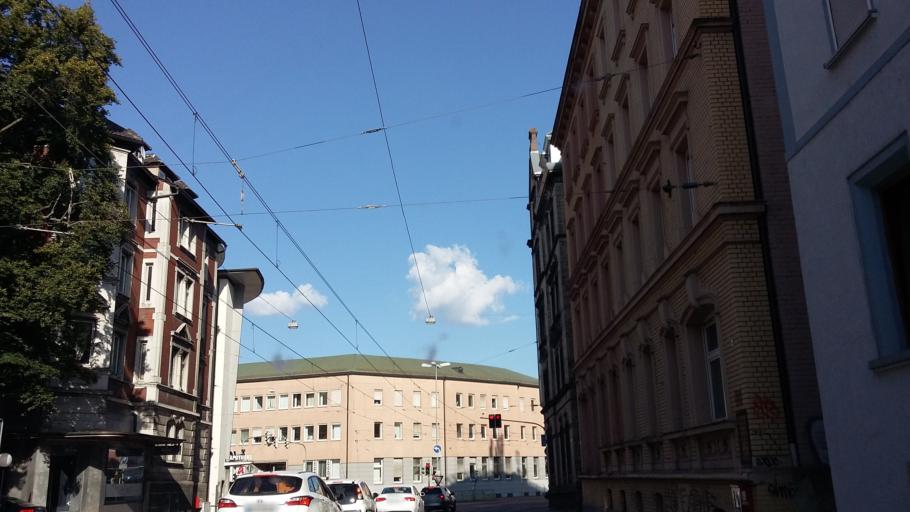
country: DE
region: Baden-Wuerttemberg
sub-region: Tuebingen Region
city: Ulm
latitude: 48.4026
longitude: 9.9986
